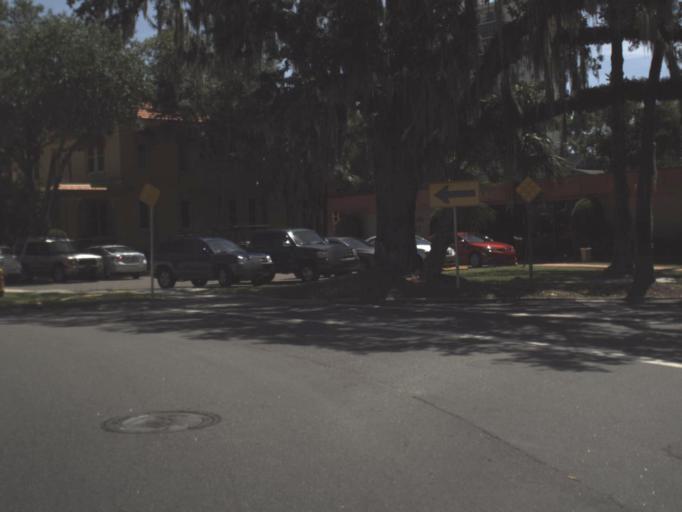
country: US
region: Florida
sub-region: Duval County
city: Jacksonville
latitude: 30.3115
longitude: -81.6789
